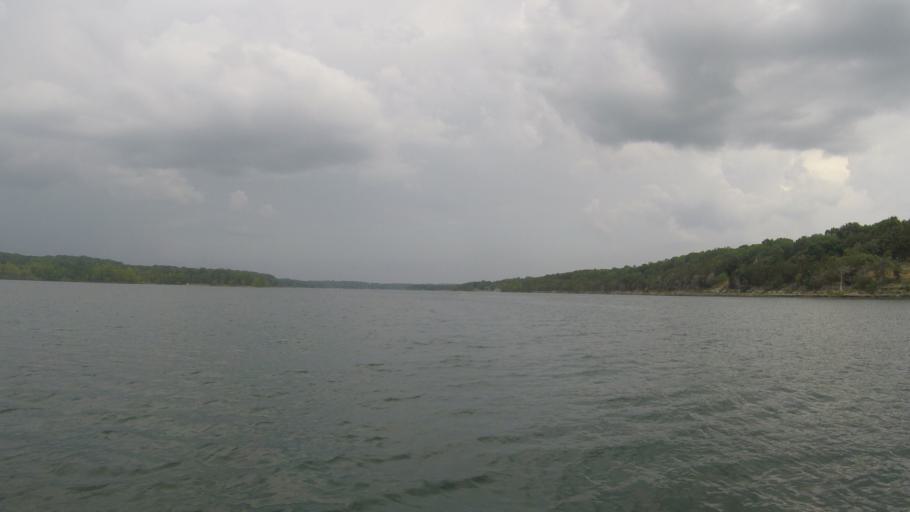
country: US
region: Missouri
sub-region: Barry County
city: Shell Knob
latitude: 36.5907
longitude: -93.5428
